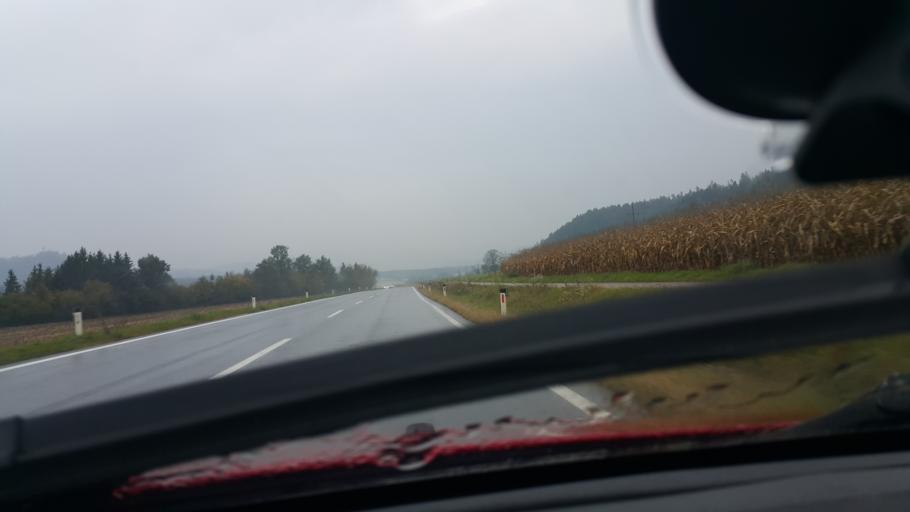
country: AT
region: Carinthia
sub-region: Politischer Bezirk Volkermarkt
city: Ruden
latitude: 46.6405
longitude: 14.7759
